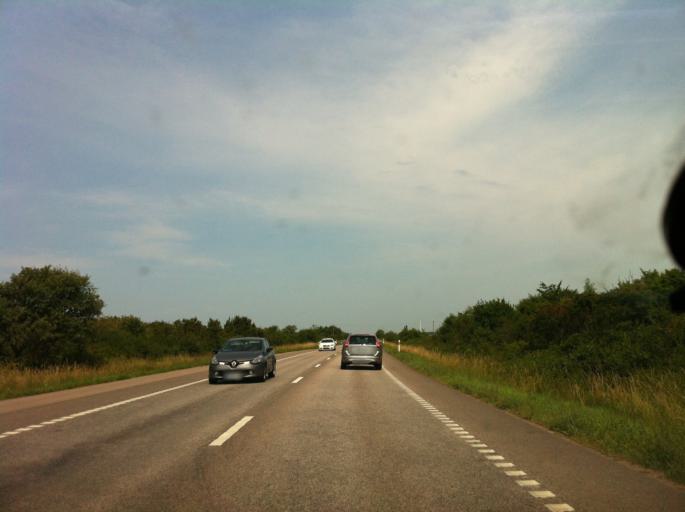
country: SE
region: Kalmar
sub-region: Borgholms Kommun
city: Borgholm
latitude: 56.8206
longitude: 16.6054
